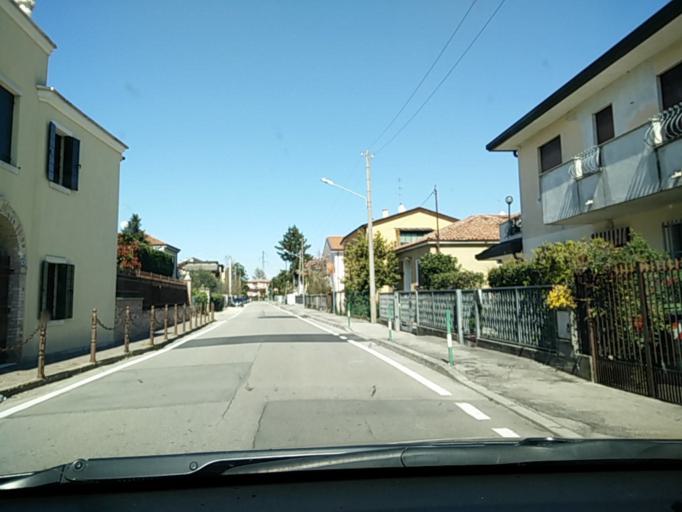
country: IT
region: Veneto
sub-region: Provincia di Padova
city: Caselle
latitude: 45.4157
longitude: 11.8345
